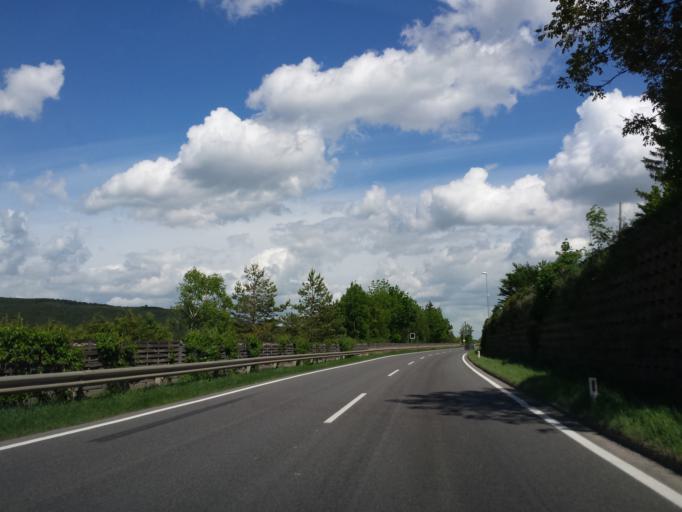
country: AT
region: Lower Austria
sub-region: Politischer Bezirk Baden
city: Hernstein
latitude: 47.8709
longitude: 16.0900
